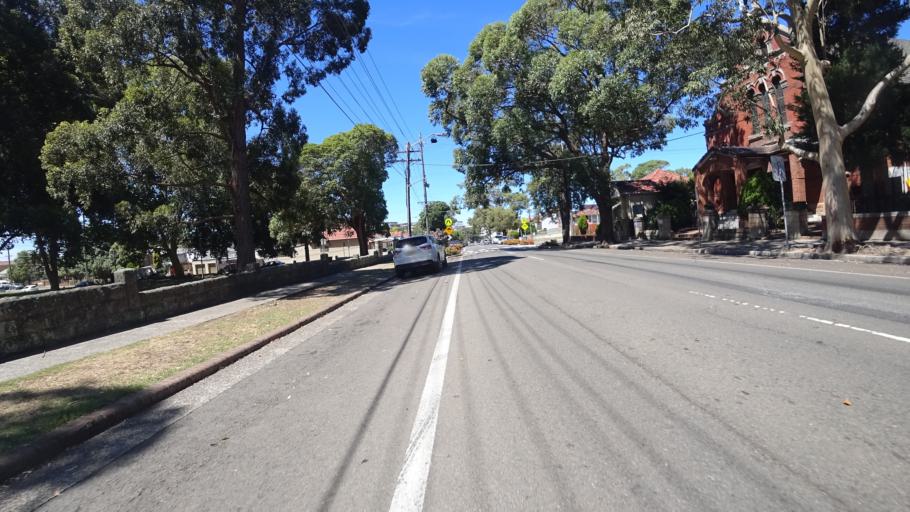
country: AU
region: New South Wales
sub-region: Rockdale
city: Arncliffe
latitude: -33.9359
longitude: 151.1434
